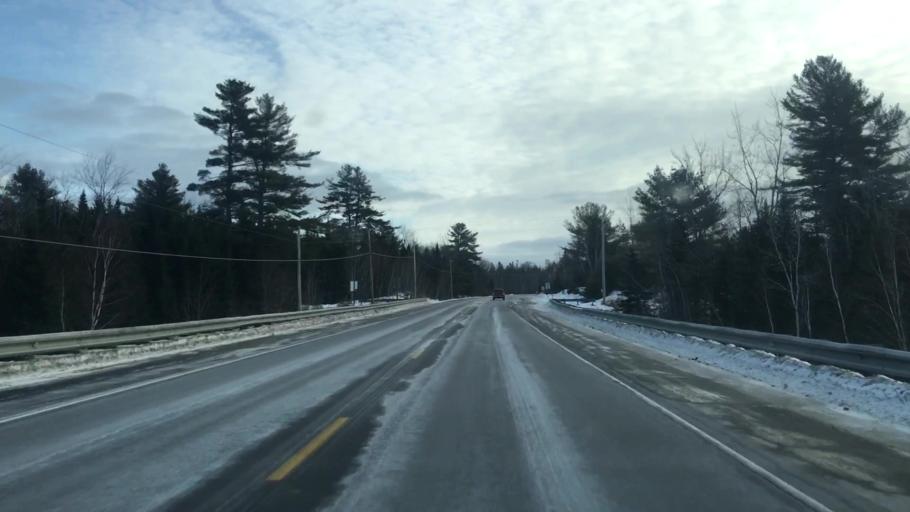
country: US
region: Maine
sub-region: Washington County
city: Machias
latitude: 44.9503
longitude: -67.6767
